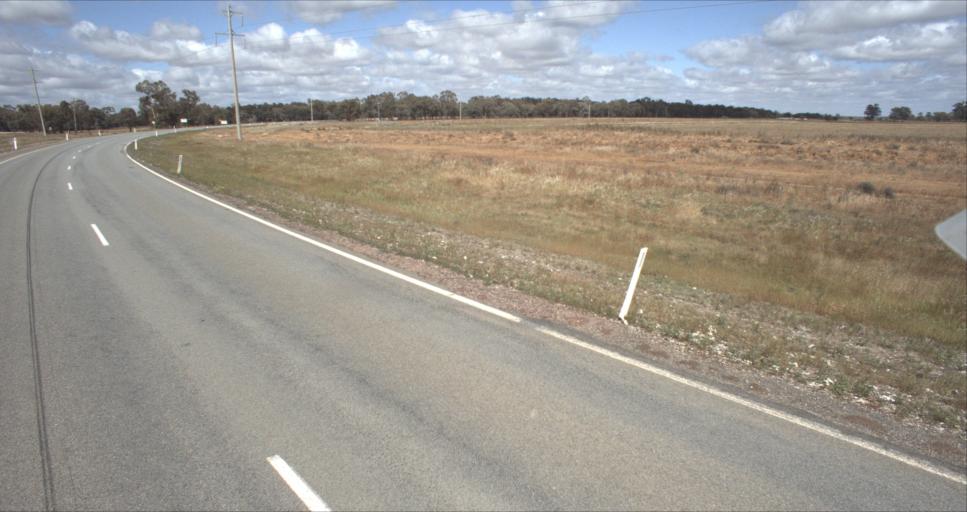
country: AU
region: New South Wales
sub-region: Murrumbidgee Shire
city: Darlington Point
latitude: -34.5952
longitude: 146.1628
